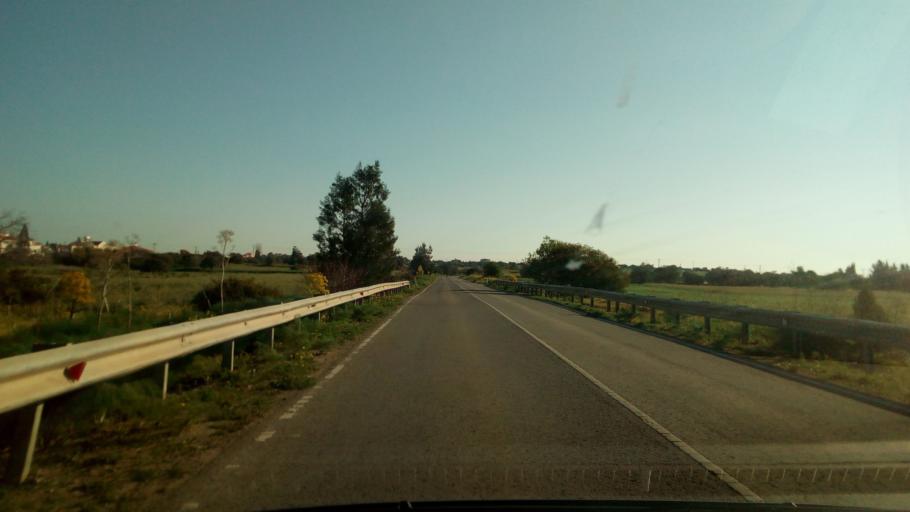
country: CY
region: Larnaka
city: Tersefanou
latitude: 34.7945
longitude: 33.4918
